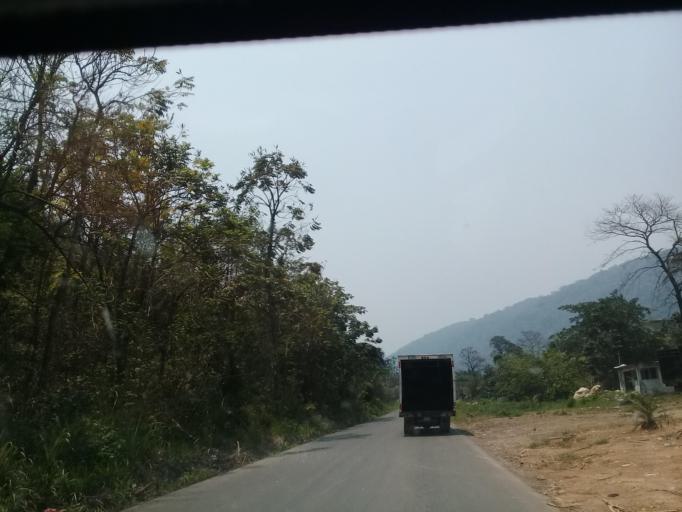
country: MX
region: Veracruz
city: Tezonapa
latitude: 18.6102
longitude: -96.6931
